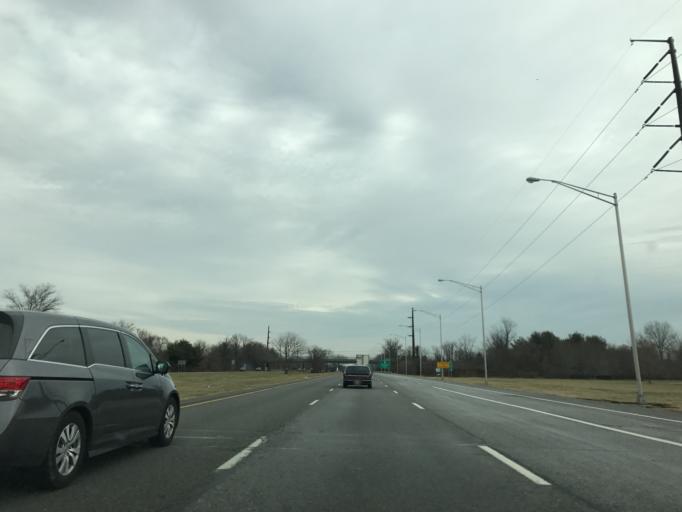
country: US
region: New Jersey
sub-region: Salem County
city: Carneys Point
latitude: 39.7026
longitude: -75.4573
